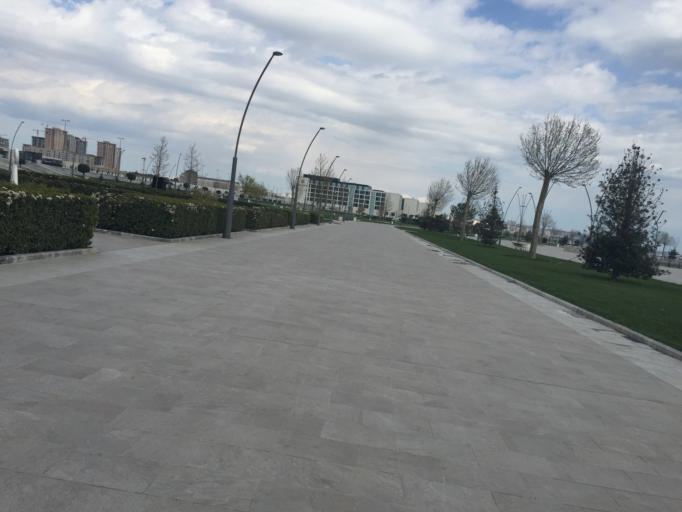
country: AZ
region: Baki
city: Baku
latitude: 40.3751
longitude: 49.8772
